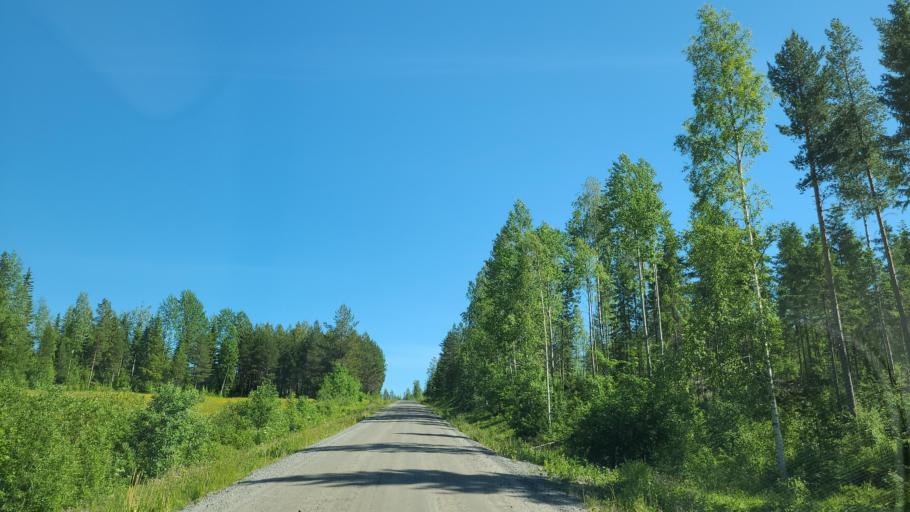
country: SE
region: Vaesterbotten
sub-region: Bjurholms Kommun
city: Bjurholm
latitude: 63.6420
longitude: 19.1005
